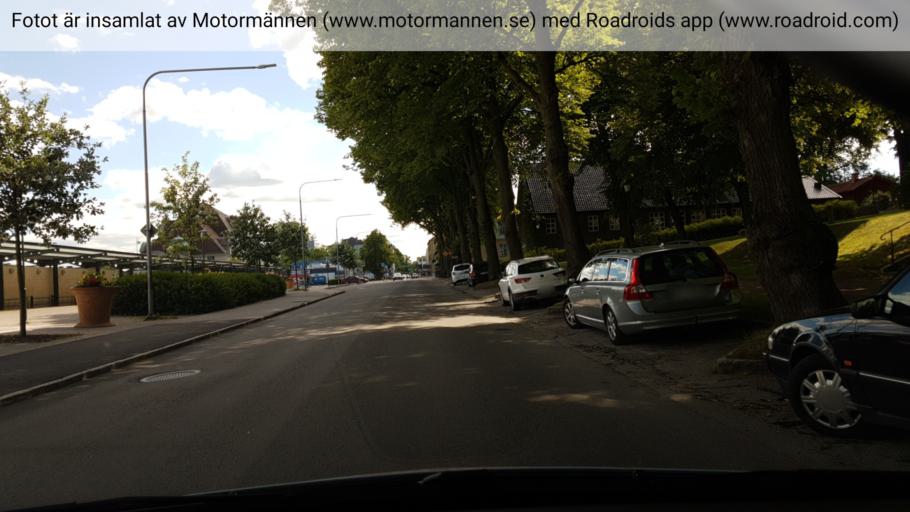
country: SE
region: Vaestra Goetaland
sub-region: Mariestads Kommun
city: Mariestad
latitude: 58.7126
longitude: 13.8240
